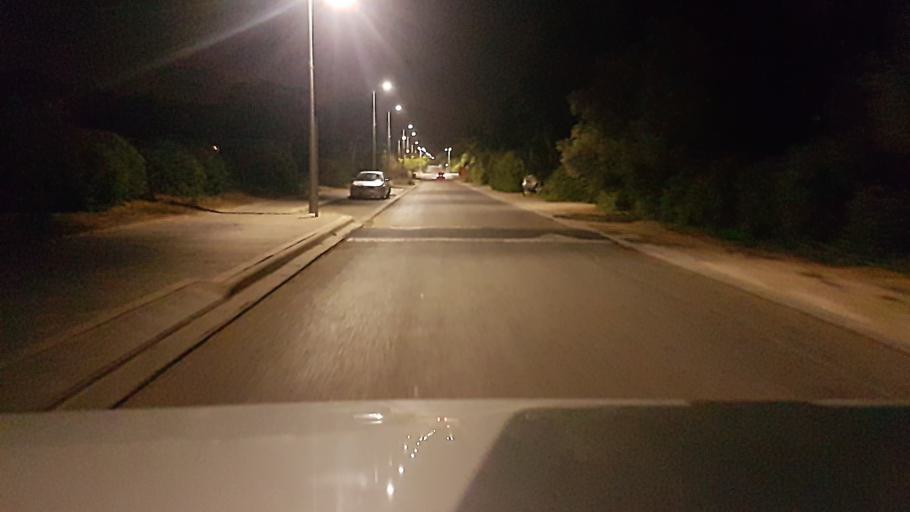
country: IL
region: Central District
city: Nehalim
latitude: 32.0779
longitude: 34.9231
